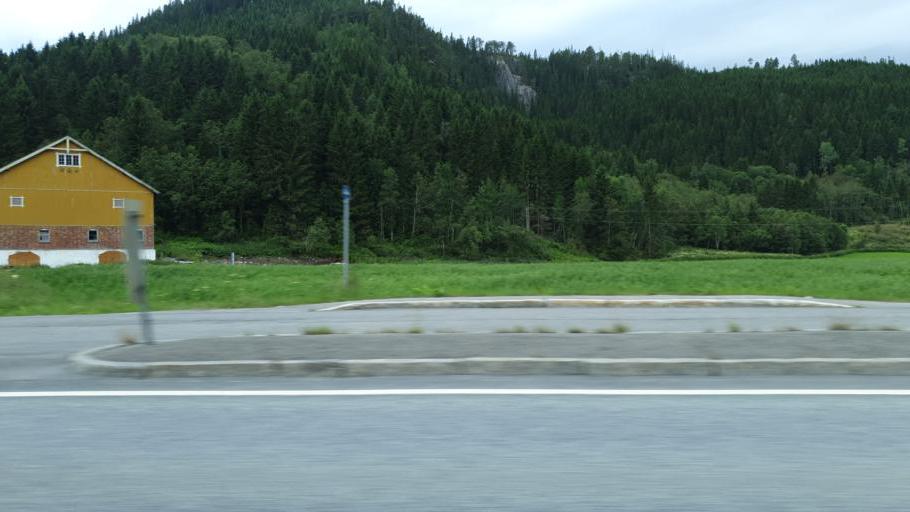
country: NO
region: Sor-Trondelag
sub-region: Midtre Gauldal
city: Storen
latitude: 63.0149
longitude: 10.2464
